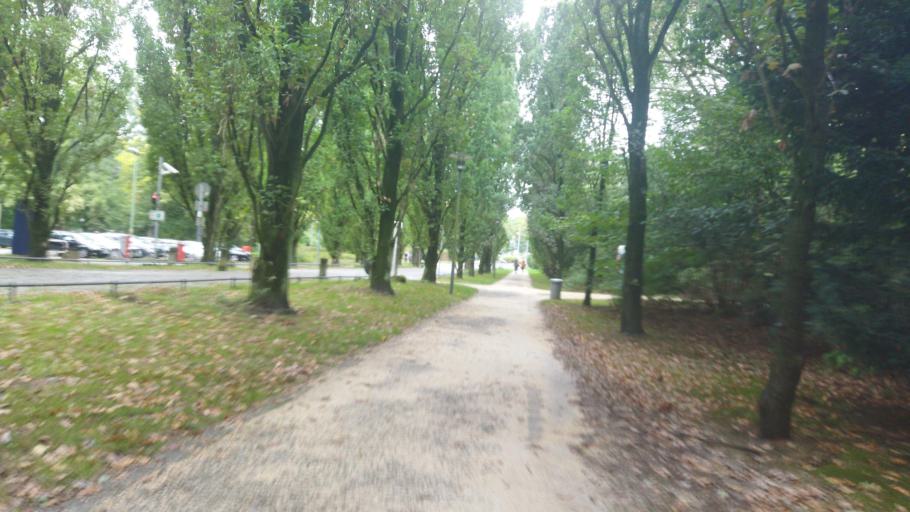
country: DE
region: North Rhine-Westphalia
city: Herten
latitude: 51.5925
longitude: 7.1281
